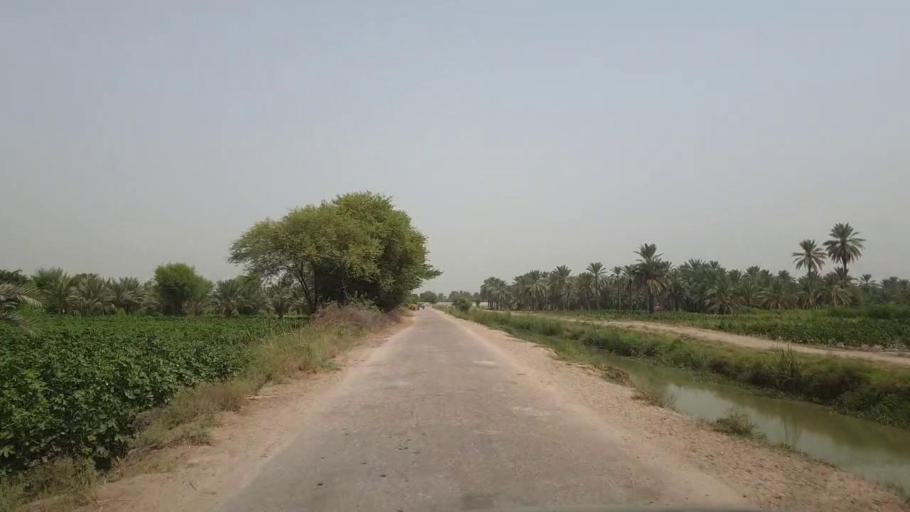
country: PK
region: Sindh
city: Gambat
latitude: 27.4336
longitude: 68.5604
